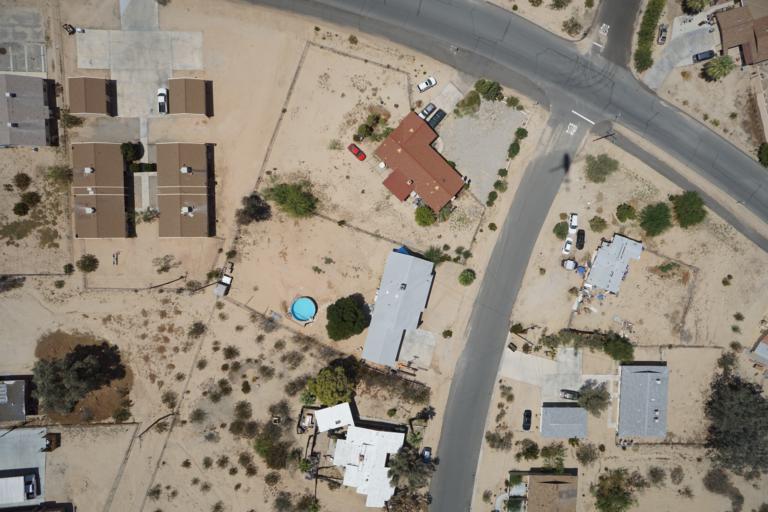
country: US
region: California
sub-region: San Bernardino County
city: Twentynine Palms
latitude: 34.1484
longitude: -116.0572
